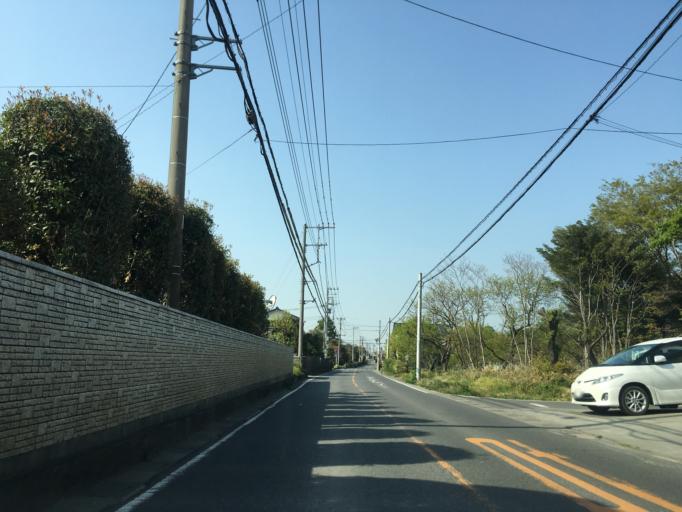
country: JP
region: Saitama
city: Ageoshimo
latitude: 35.9771
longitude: 139.6332
